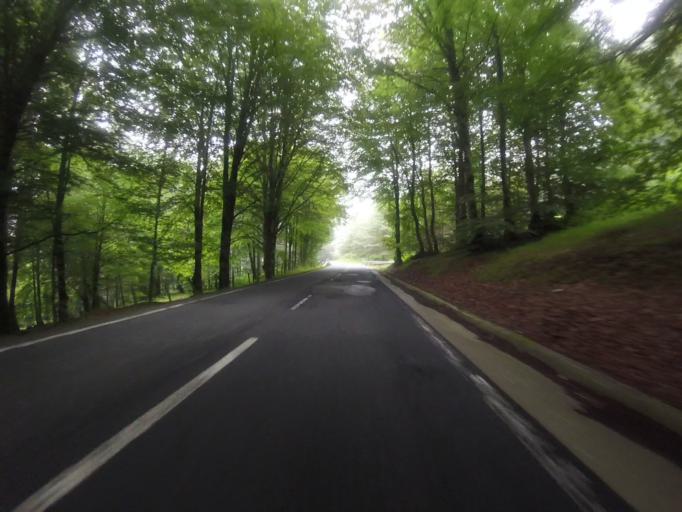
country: ES
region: Navarre
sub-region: Provincia de Navarra
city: Ezkurra
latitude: 43.0827
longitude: -1.8605
